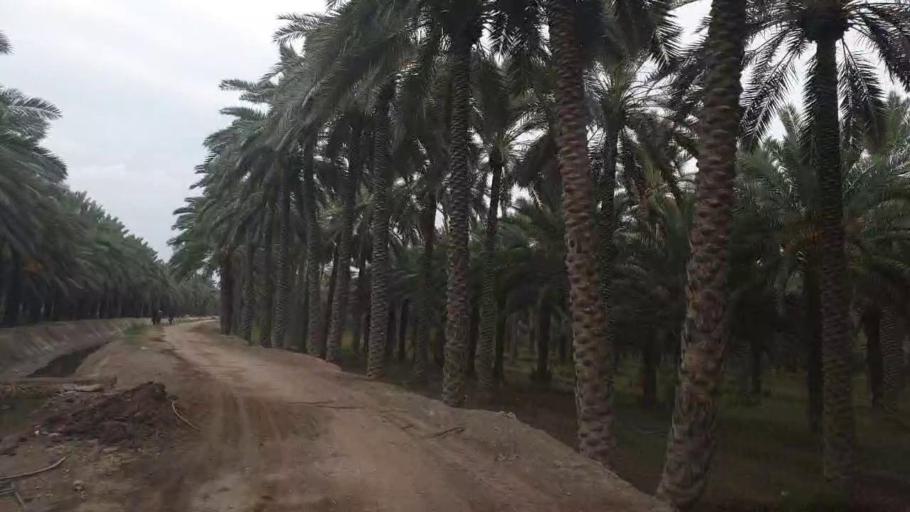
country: PK
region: Sindh
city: Khairpur
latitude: 27.5954
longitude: 68.8006
